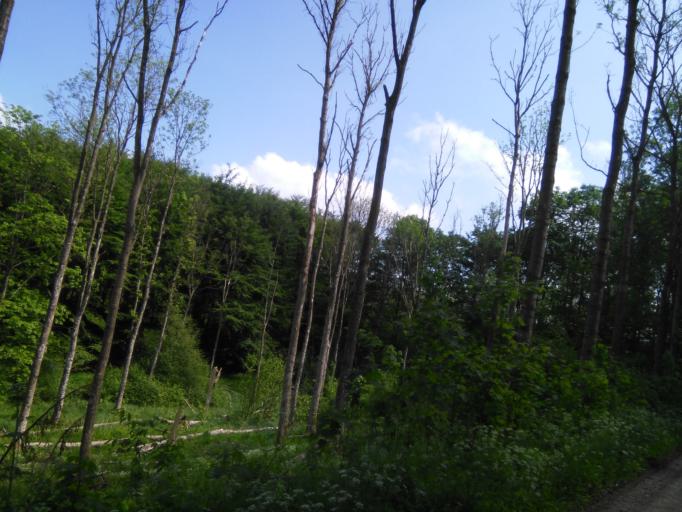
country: DK
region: Central Jutland
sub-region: Favrskov Kommune
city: Hinnerup
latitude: 56.2712
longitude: 10.0204
